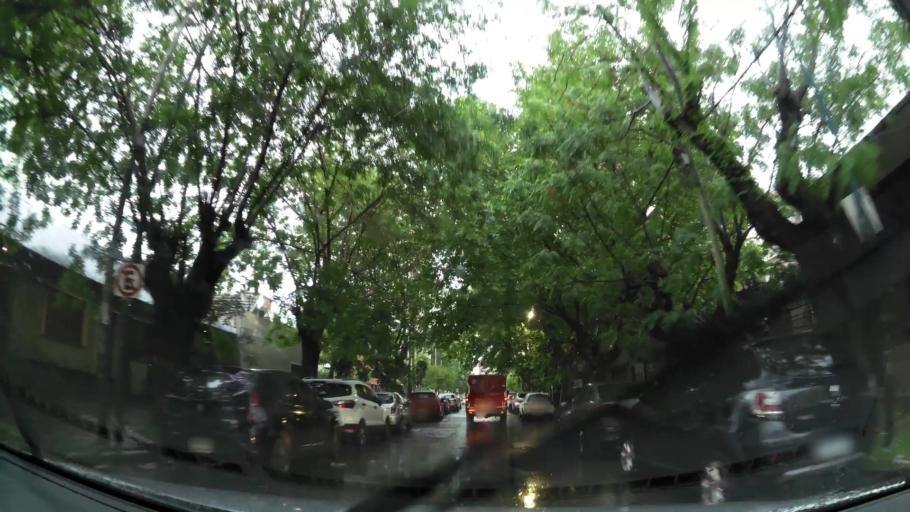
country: AR
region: Buenos Aires
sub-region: Partido de Lanus
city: Lanus
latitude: -34.7100
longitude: -58.3943
